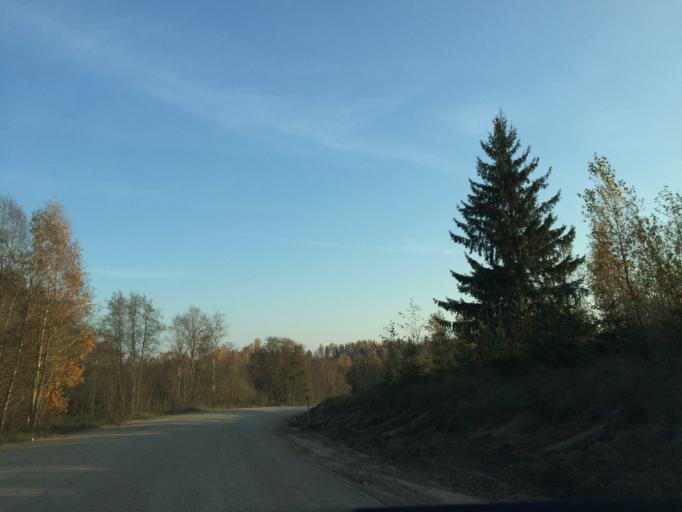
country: LV
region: Vainode
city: Vainode
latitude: 56.5827
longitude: 21.8463
